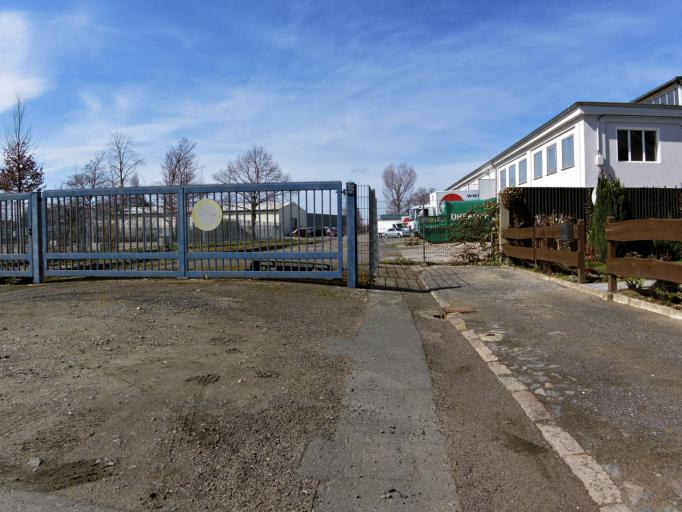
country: DE
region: Saxony
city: Taucha
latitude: 51.3415
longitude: 12.4877
